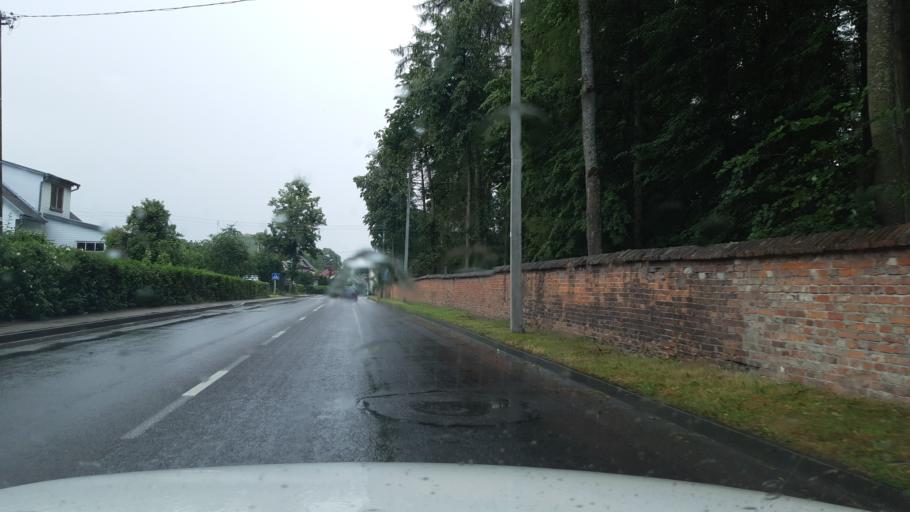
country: LT
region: Taurages apskritis
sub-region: Jurbarkas
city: Jurbarkas
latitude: 55.0814
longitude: 22.7563
